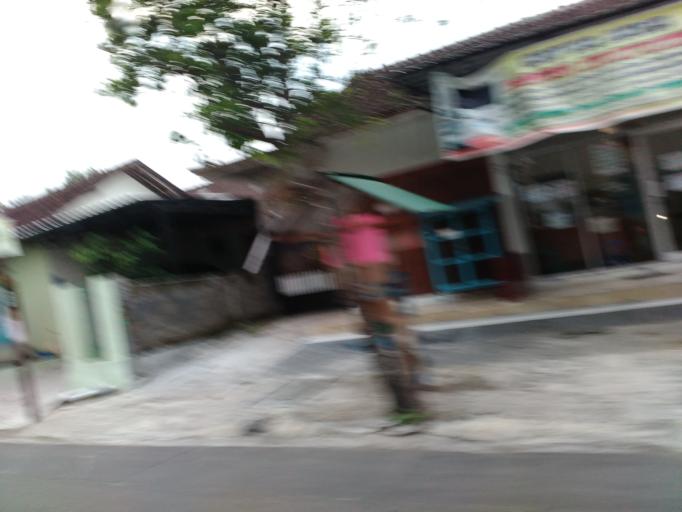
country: ID
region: Central Java
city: Boyolali
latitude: -7.5258
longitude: 110.5942
